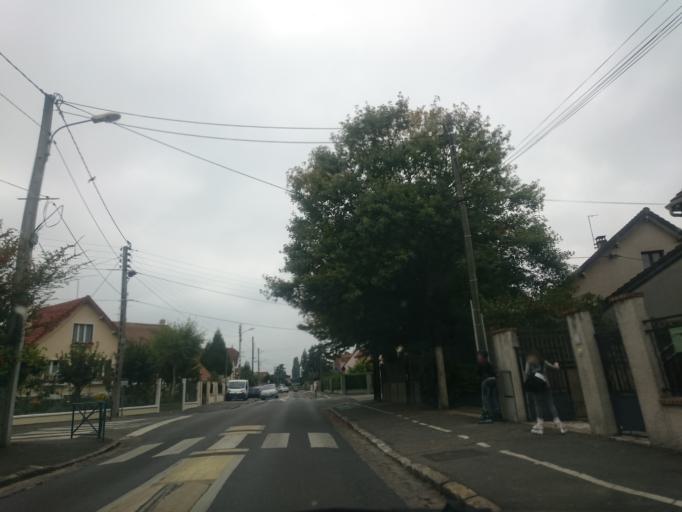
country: FR
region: Ile-de-France
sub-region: Departement de l'Essonne
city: Sainte-Genevieve-des-Bois
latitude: 48.6459
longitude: 2.3386
